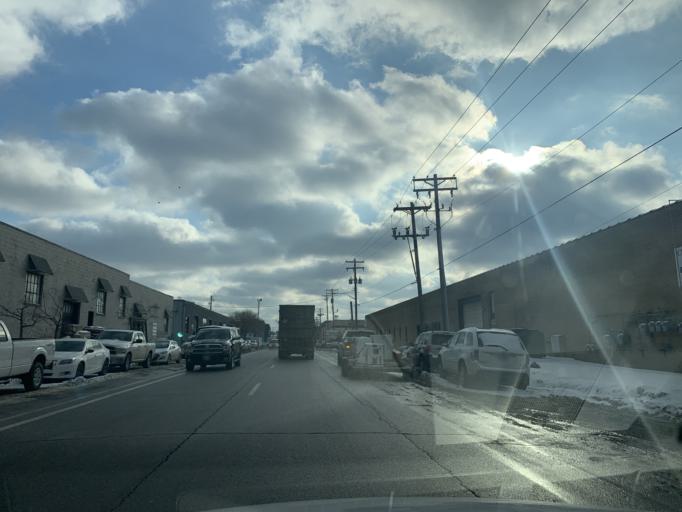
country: US
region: Minnesota
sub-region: Hennepin County
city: Minneapolis
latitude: 45.0048
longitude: -93.2803
